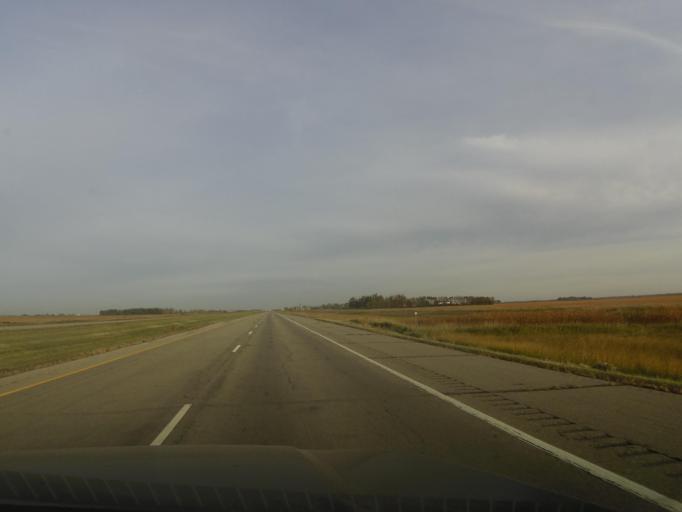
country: US
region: Minnesota
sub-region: Kittson County
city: Hallock
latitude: 48.7451
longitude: -97.1984
